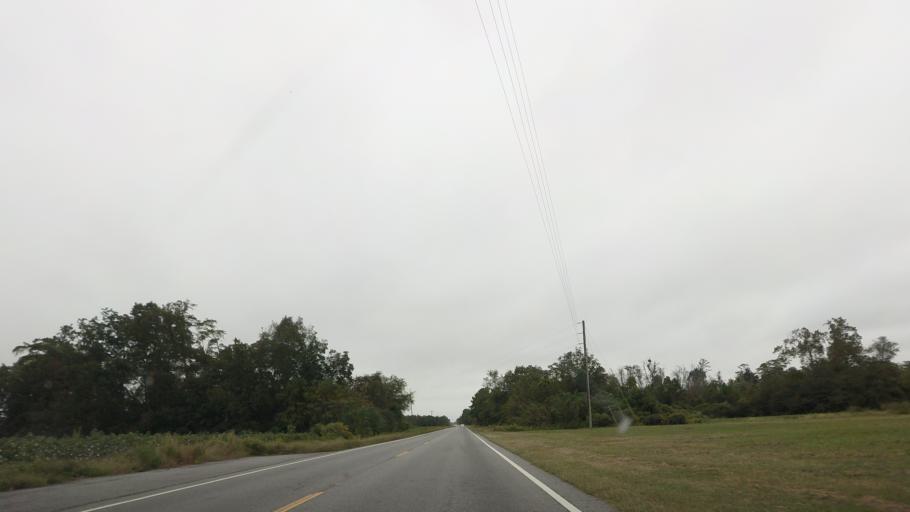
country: US
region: Georgia
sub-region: Berrien County
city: Nashville
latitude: 31.3308
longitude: -83.2299
